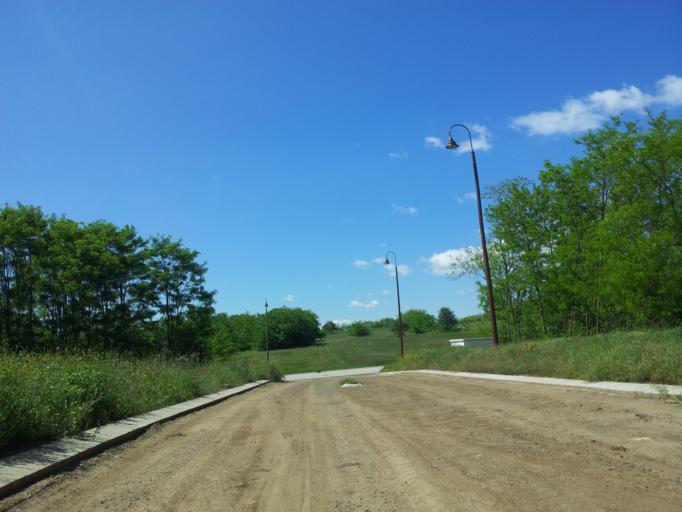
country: HU
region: Pest
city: Orbottyan
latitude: 47.6711
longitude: 19.2786
